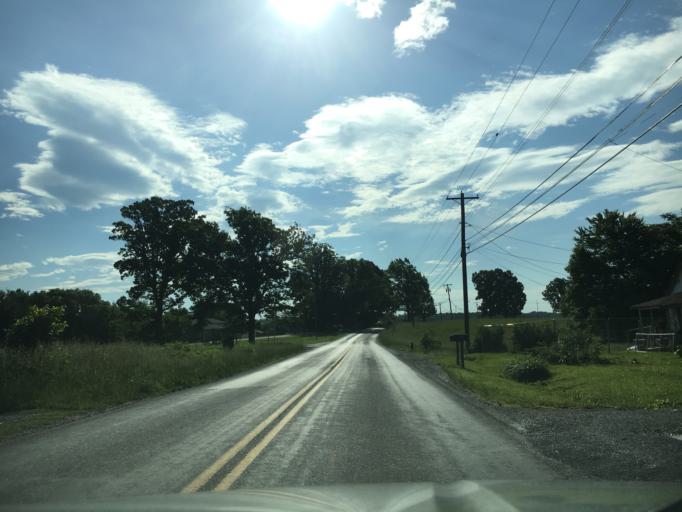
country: US
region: Virginia
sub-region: Campbell County
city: Timberlake
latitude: 37.3306
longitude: -79.2055
